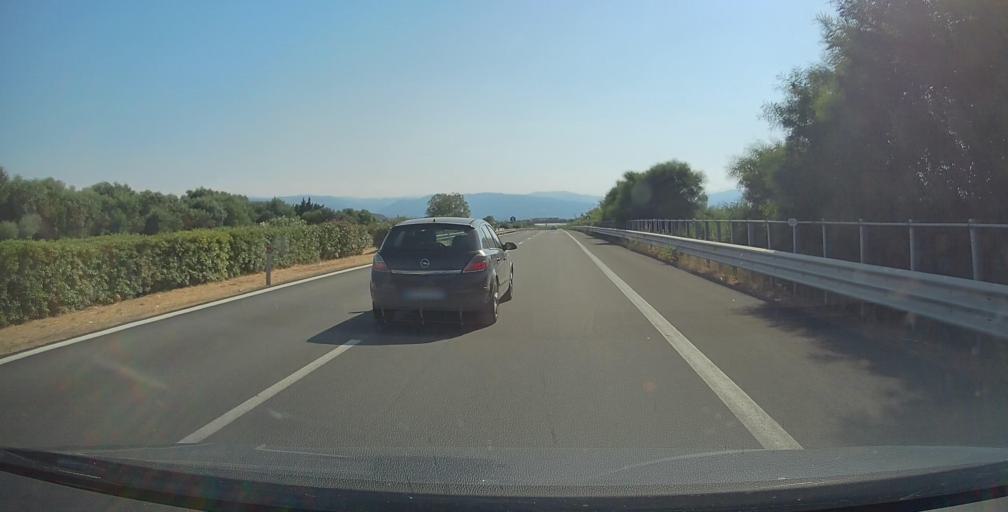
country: IT
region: Sicily
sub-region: Messina
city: Terme
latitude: 38.1379
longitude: 15.1518
